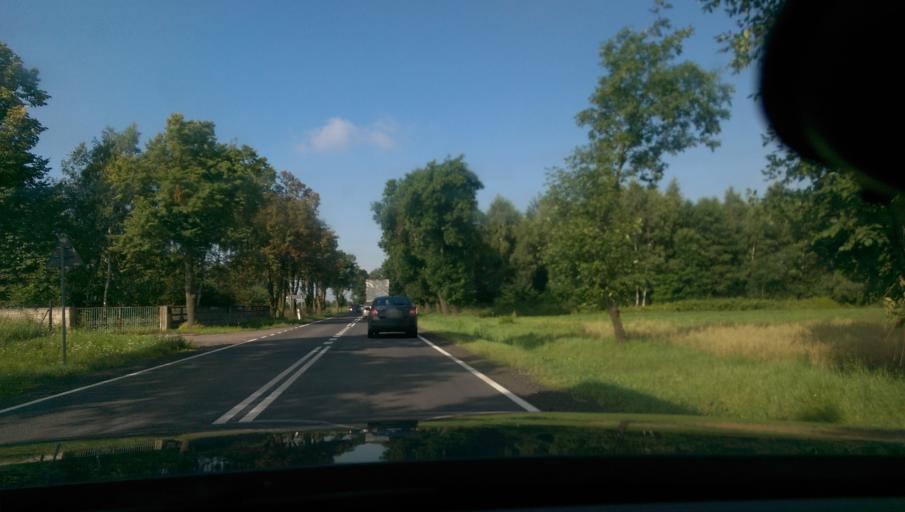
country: PL
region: Masovian Voivodeship
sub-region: Powiat plonski
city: Plonsk
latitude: 52.6461
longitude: 20.4200
